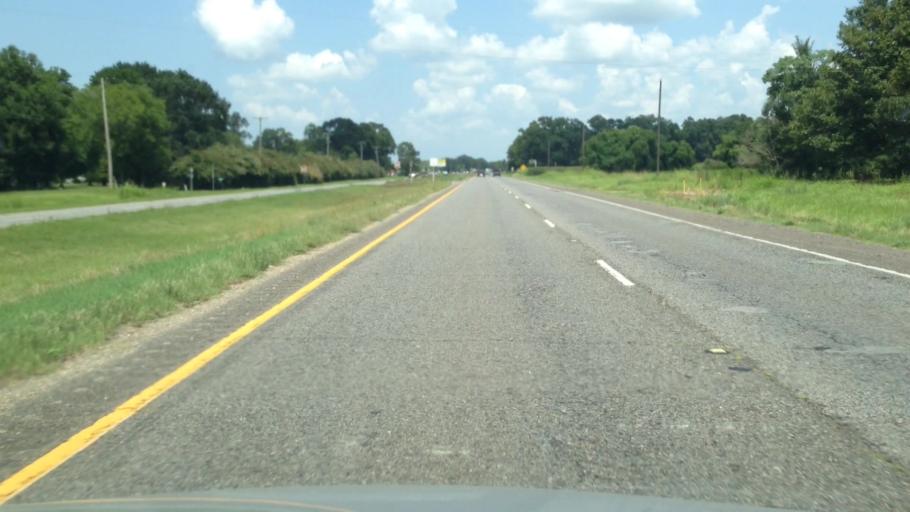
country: US
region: Louisiana
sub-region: Saint Landry Parish
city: Port Barre
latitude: 30.5443
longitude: -92.0155
